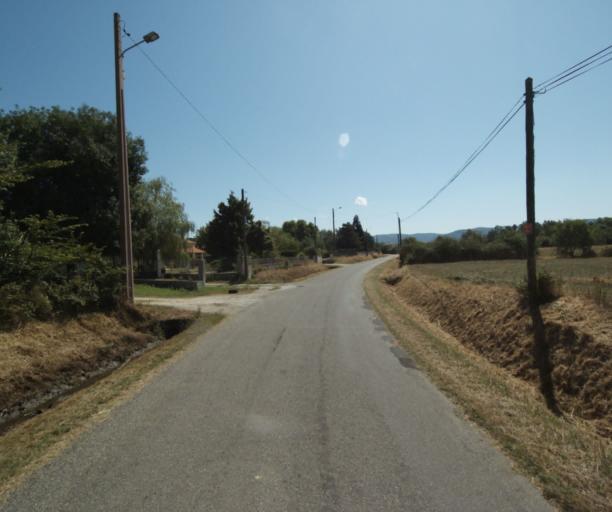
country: FR
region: Midi-Pyrenees
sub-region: Departement de la Haute-Garonne
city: Revel
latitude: 43.4730
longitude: 1.9889
